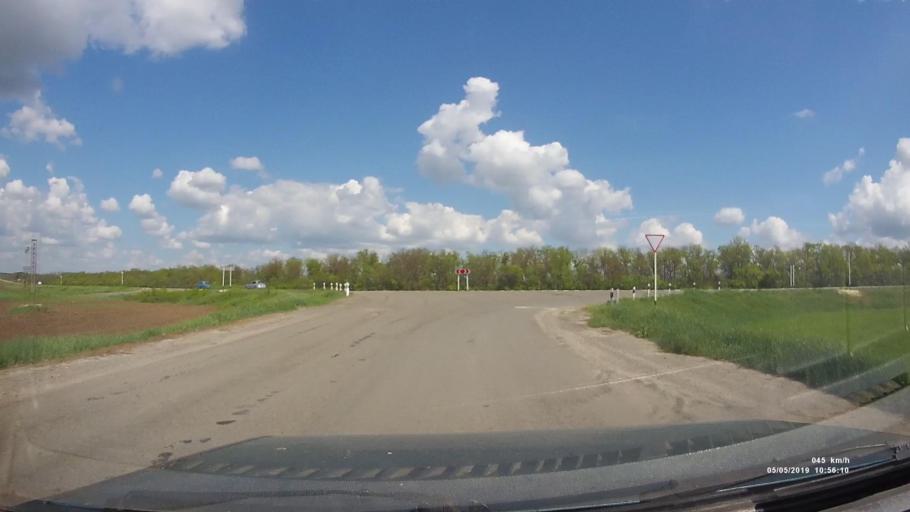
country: RU
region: Rostov
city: Ust'-Donetskiy
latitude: 47.6715
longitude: 40.8205
